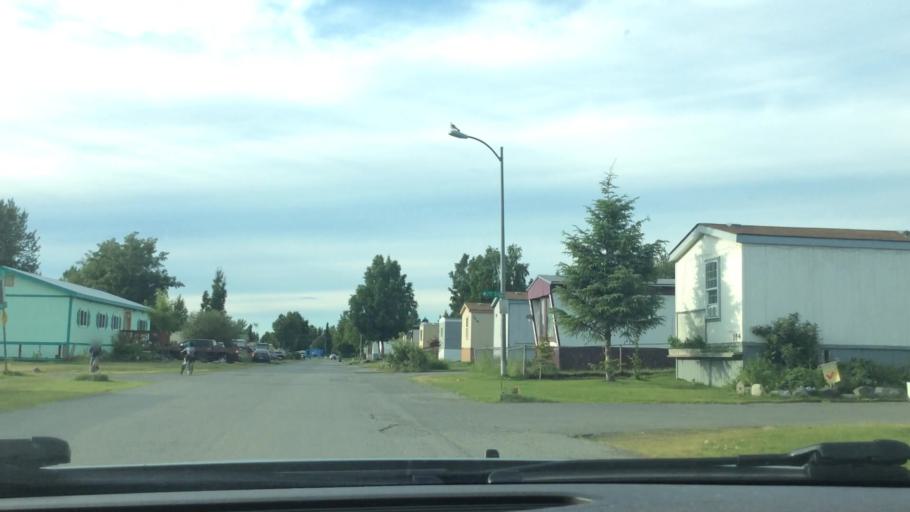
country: US
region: Alaska
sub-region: Anchorage Municipality
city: Anchorage
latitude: 61.1334
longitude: -149.8504
